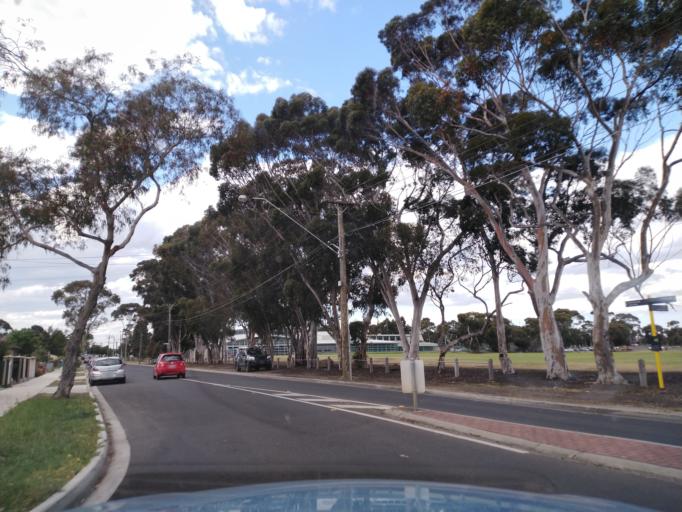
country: AU
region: Victoria
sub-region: Hobsons Bay
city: Altona North
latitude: -37.8417
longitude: 144.8546
